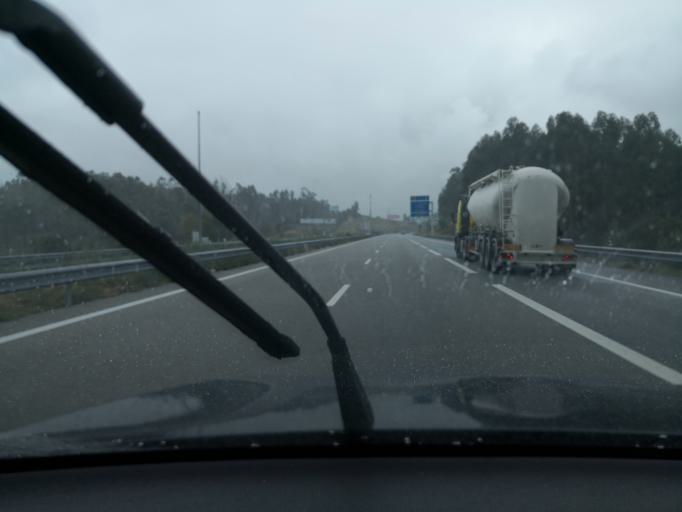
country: PT
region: Porto
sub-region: Pacos de Ferreira
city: Frazao
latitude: 41.2614
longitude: -8.3881
